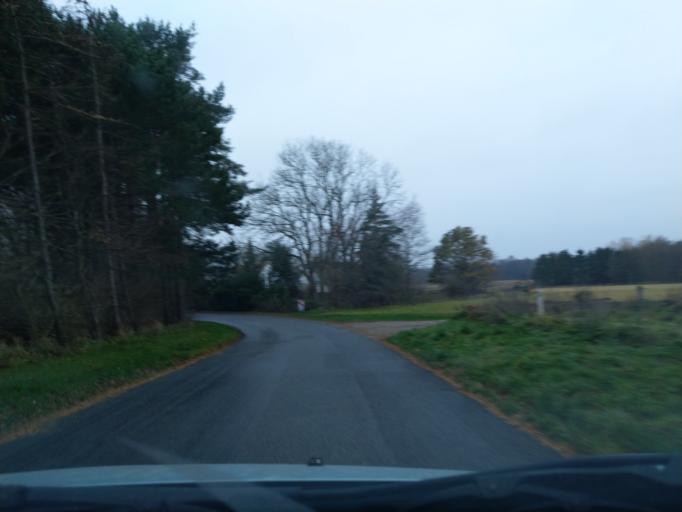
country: DK
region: Zealand
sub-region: Vordingborg Kommune
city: Praesto
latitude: 55.1186
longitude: 12.1201
